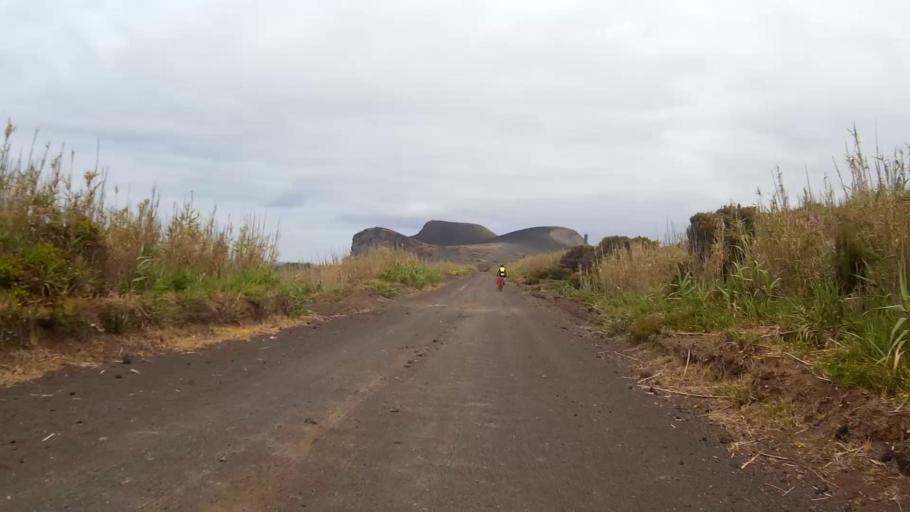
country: PT
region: Azores
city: Ribeira Grande
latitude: 38.5888
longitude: -28.8224
